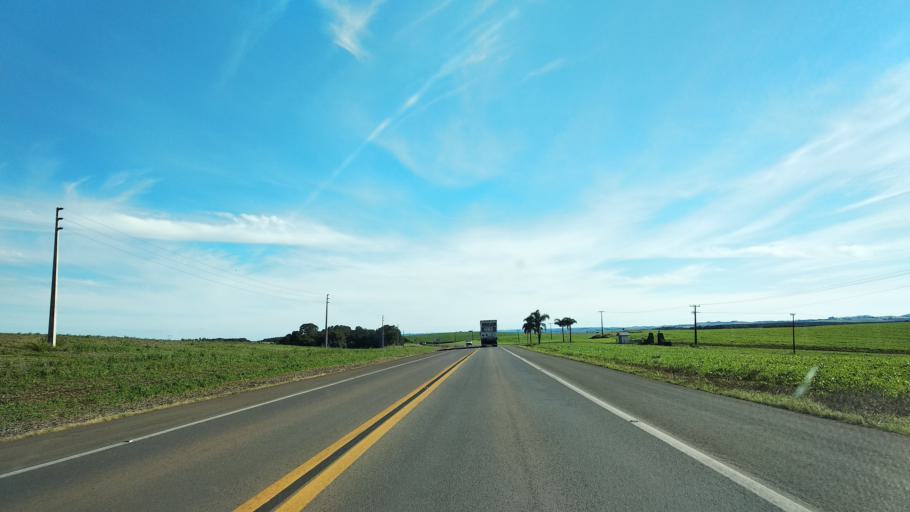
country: BR
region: Santa Catarina
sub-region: Campos Novos
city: Campos Novos
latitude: -27.4902
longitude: -51.3289
